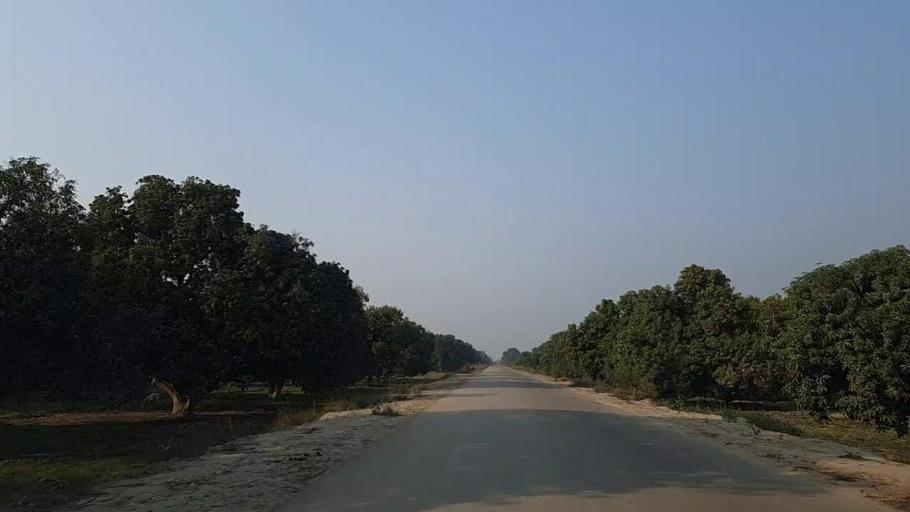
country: PK
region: Sindh
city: Sann
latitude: 26.1013
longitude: 68.1519
